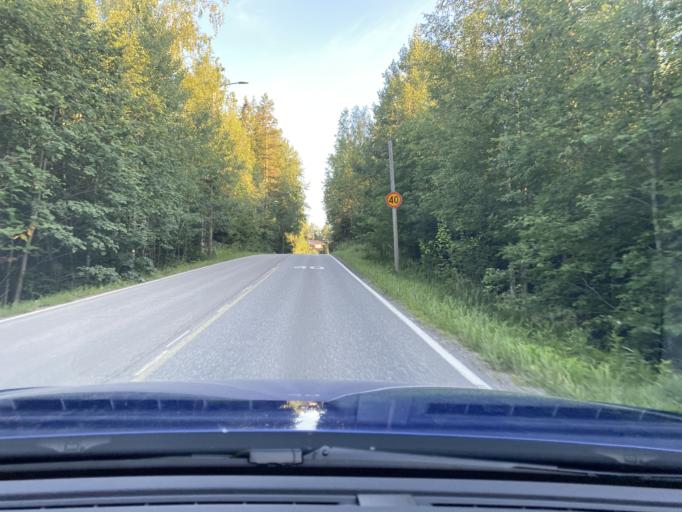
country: FI
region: Uusimaa
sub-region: Helsinki
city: Nurmijaervi
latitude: 60.4078
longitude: 24.7656
